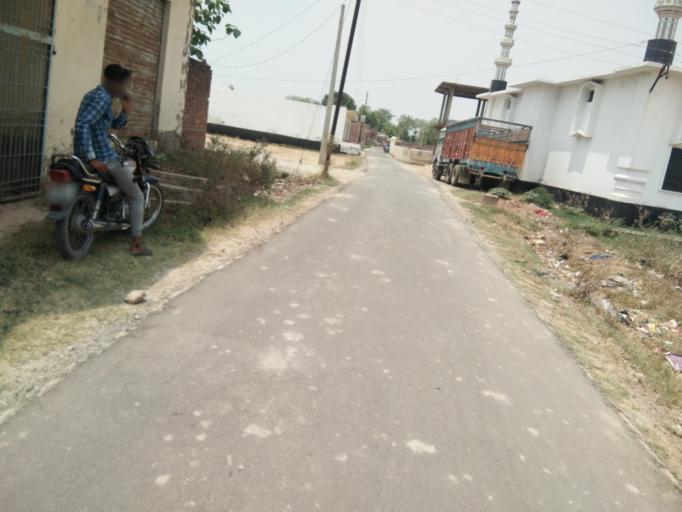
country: IN
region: Uttar Pradesh
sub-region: Ghazipur
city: Zamania
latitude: 25.4396
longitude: 83.6844
